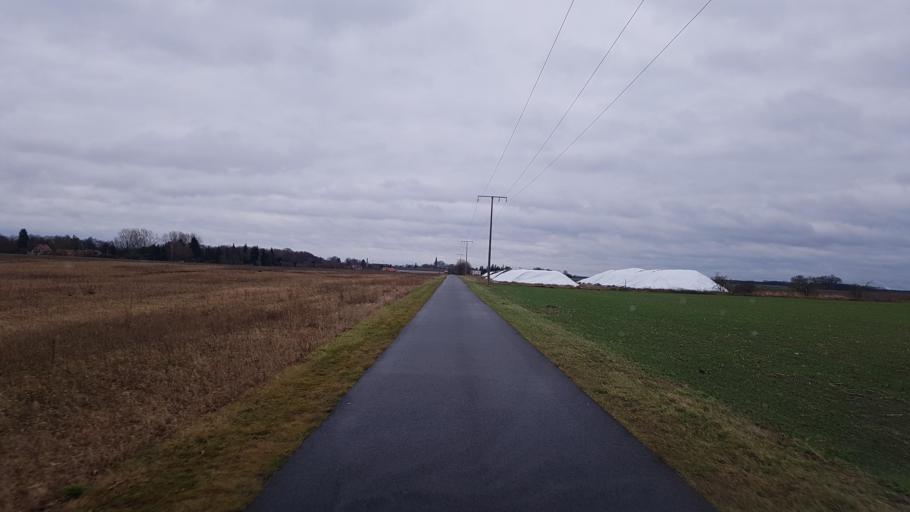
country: DE
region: Brandenburg
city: Tauche
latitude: 52.0866
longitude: 14.1496
